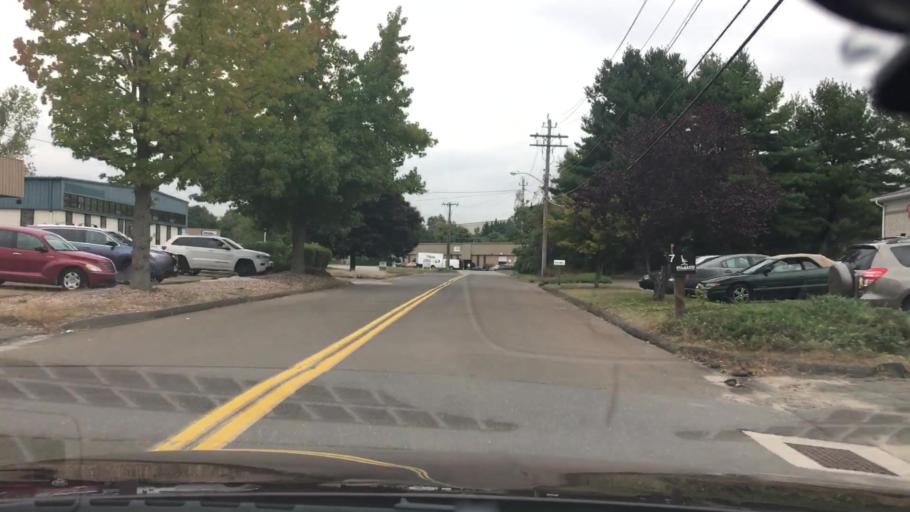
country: US
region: Connecticut
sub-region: New Haven County
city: Wallingford
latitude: 41.4783
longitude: -72.8179
